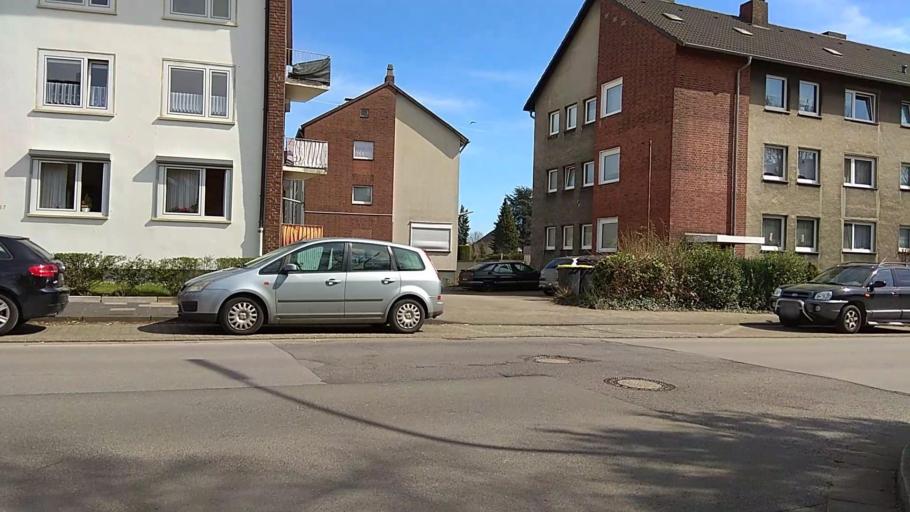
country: DE
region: North Rhine-Westphalia
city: Herten
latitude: 51.5620
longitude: 7.0911
